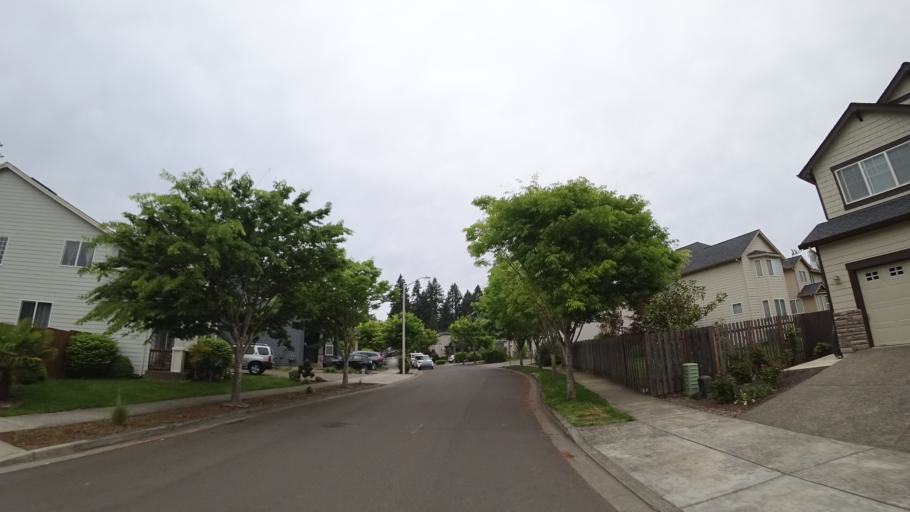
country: US
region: Oregon
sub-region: Washington County
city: Hillsboro
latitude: 45.5034
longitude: -122.9337
